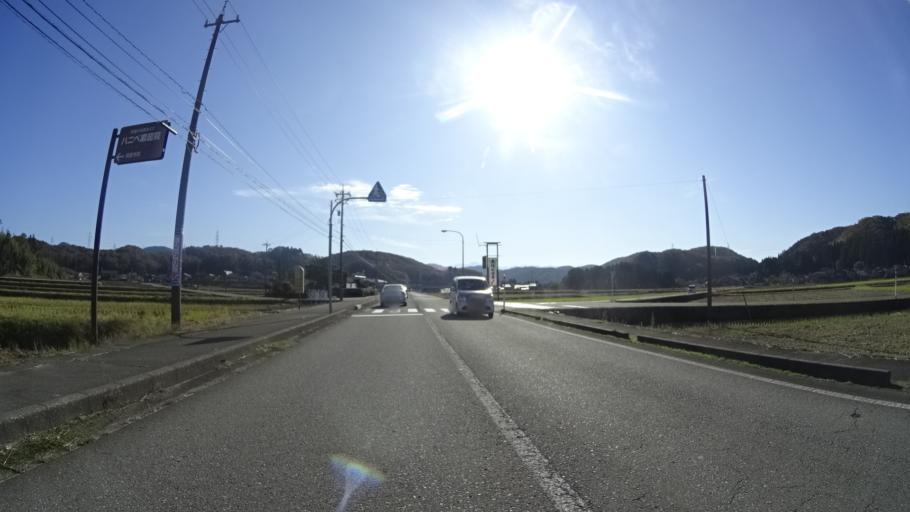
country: JP
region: Ishikawa
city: Komatsu
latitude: 36.3944
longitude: 136.5214
